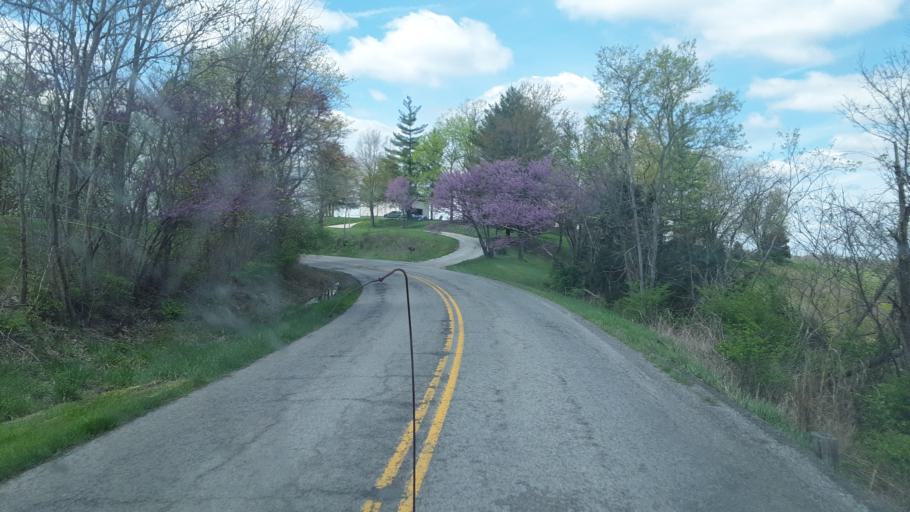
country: US
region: Kentucky
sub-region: Owen County
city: Owenton
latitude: 38.6497
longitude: -84.7403
